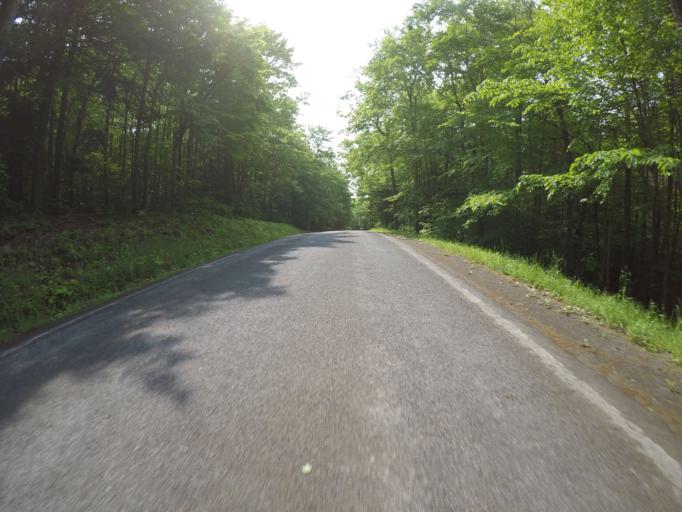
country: US
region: New York
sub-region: Delaware County
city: Stamford
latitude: 42.1559
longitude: -74.6613
